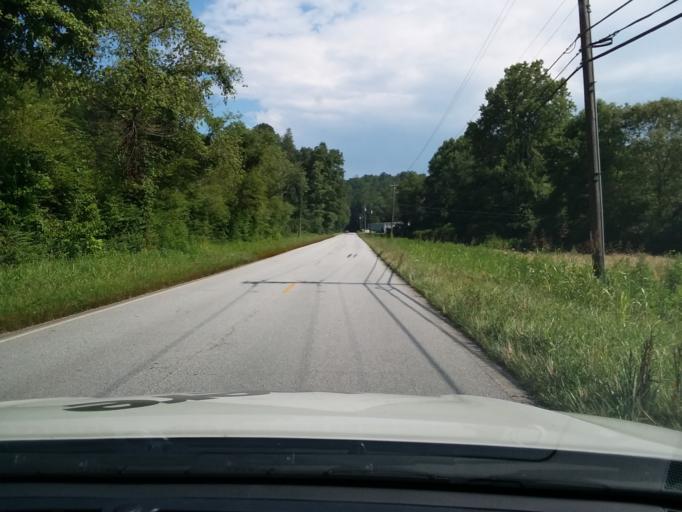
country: US
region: Georgia
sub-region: Rabun County
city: Clayton
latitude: 34.8339
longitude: -83.4325
